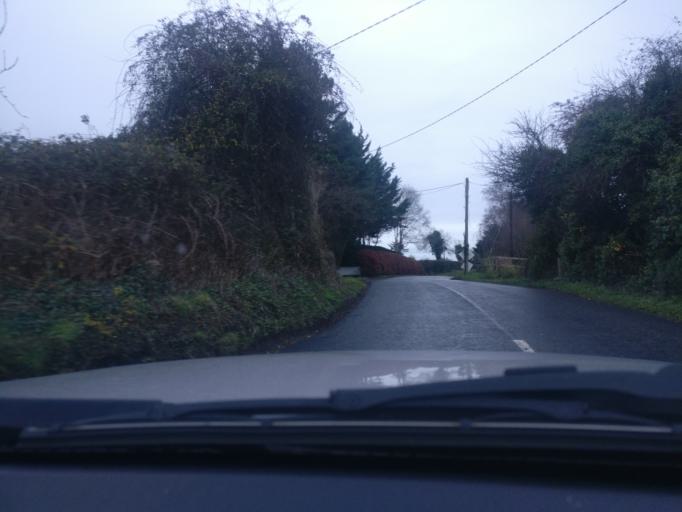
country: IE
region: Leinster
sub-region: Kildare
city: Kilcock
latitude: 53.4501
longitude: -6.6197
